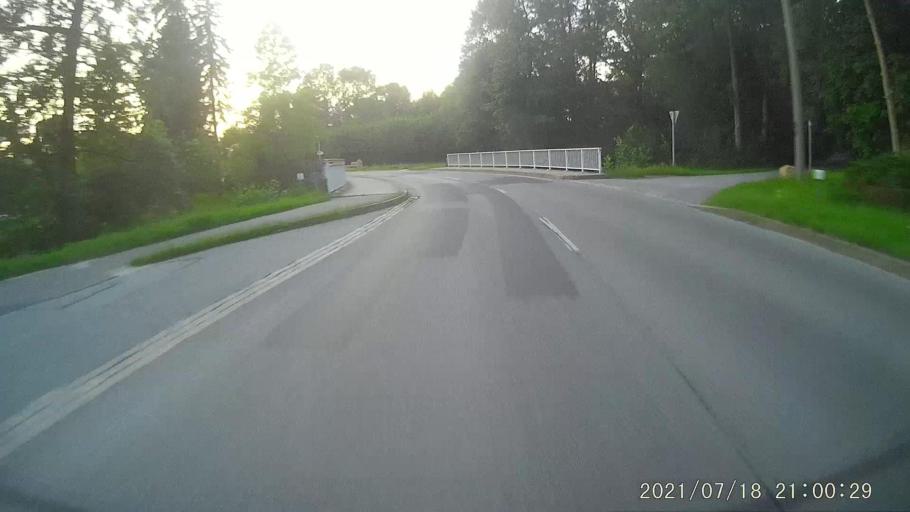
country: DE
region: Saxony
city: Goerlitz
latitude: 51.1661
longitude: 14.9361
